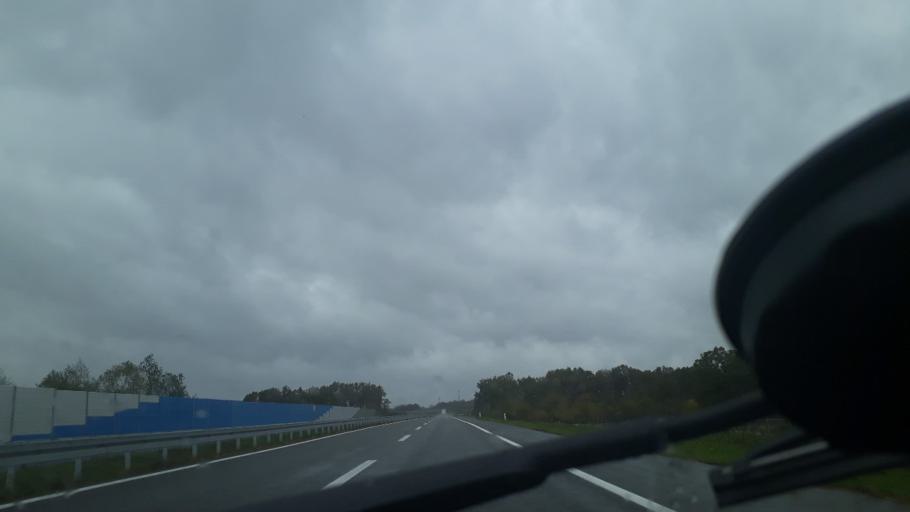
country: BA
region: Republika Srpska
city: Laktasi
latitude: 44.9891
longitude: 17.2520
